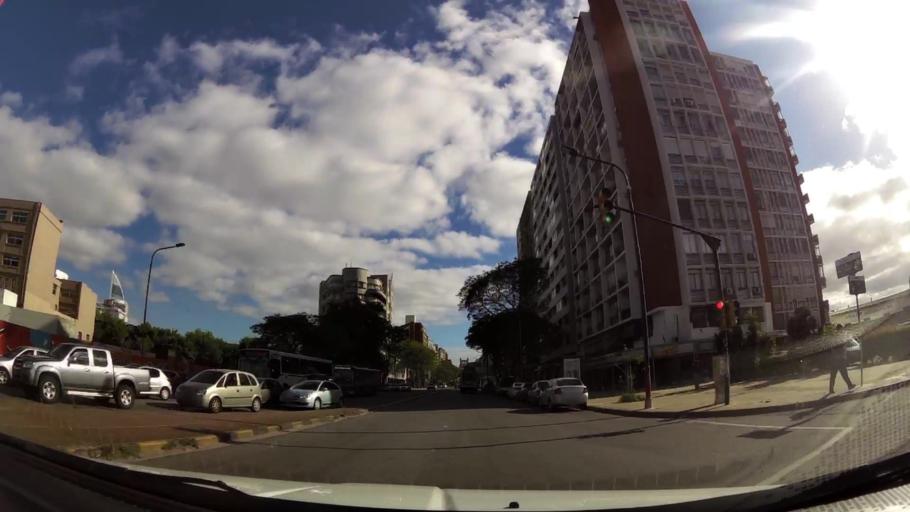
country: UY
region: Montevideo
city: Montevideo
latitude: -34.8992
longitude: -56.1911
